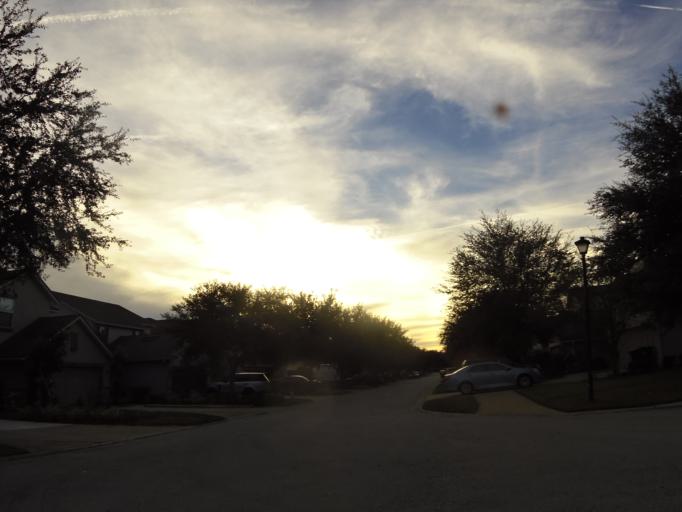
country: US
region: Florida
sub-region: Saint Johns County
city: Fruit Cove
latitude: 30.1572
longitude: -81.5457
